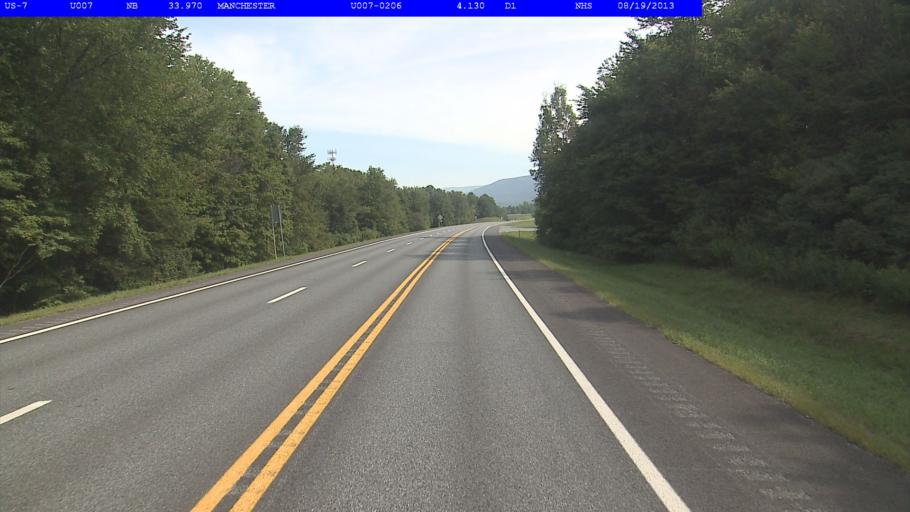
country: US
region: Vermont
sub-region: Bennington County
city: Manchester Center
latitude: 43.1681
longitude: -73.0383
